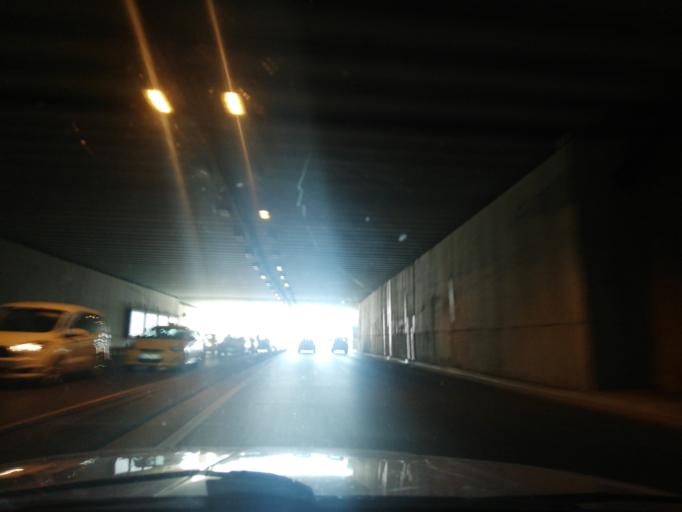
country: TR
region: Istanbul
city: Umraniye
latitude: 41.0949
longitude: 29.0965
